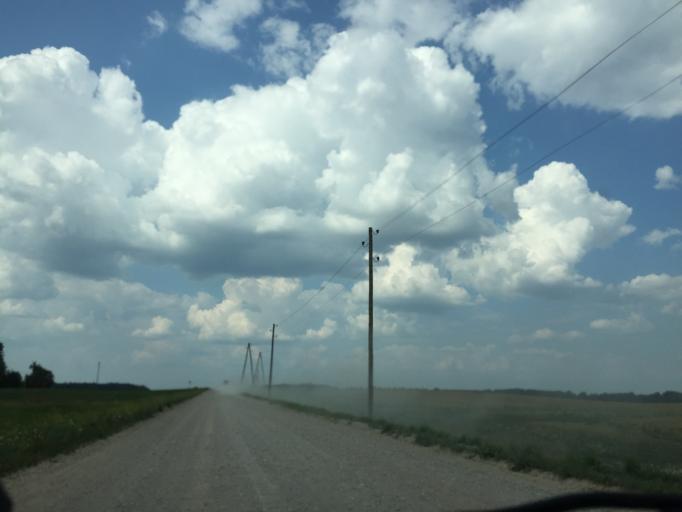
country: LT
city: Naujoji Akmene
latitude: 56.3542
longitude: 23.0581
